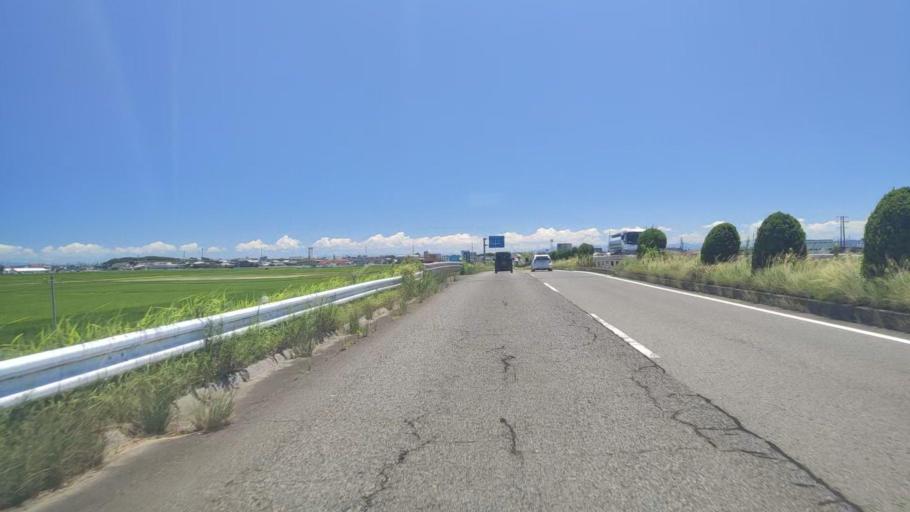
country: JP
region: Mie
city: Suzuka
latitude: 34.8814
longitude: 136.5970
